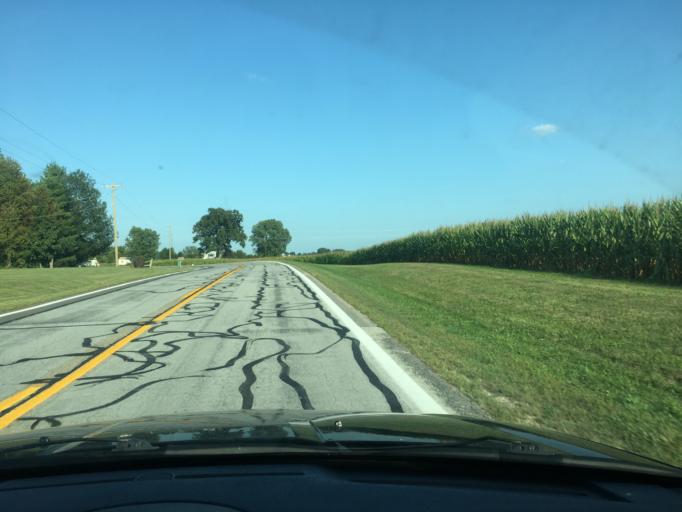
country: US
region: Ohio
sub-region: Logan County
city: West Liberty
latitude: 40.2461
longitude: -83.8006
